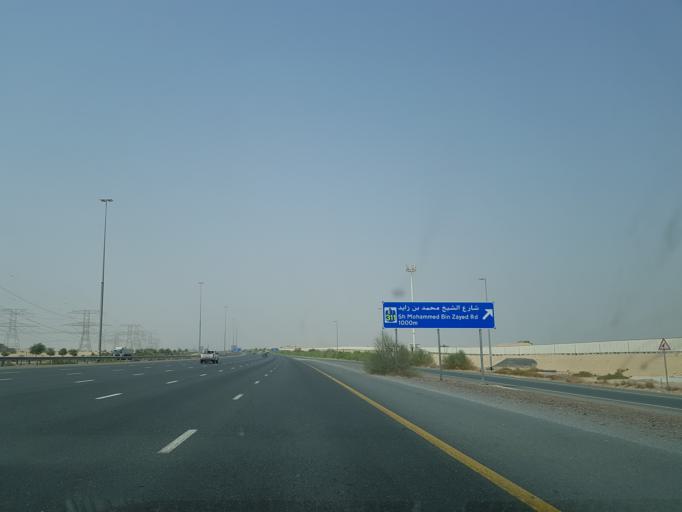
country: AE
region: Dubai
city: Dubai
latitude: 25.0591
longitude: 55.3202
